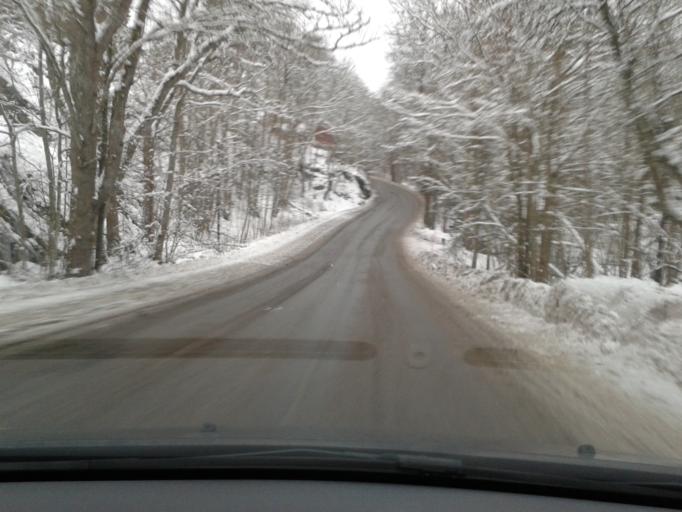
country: SE
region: Stockholm
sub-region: Nacka Kommun
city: Saltsjobaden
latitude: 59.2353
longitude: 18.2947
